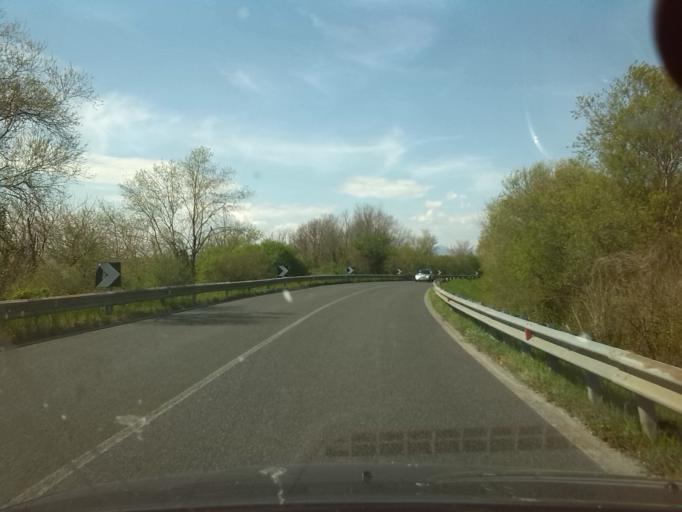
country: IT
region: Friuli Venezia Giulia
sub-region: Provincia di Udine
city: Pagnacco
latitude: 46.1073
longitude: 13.1976
